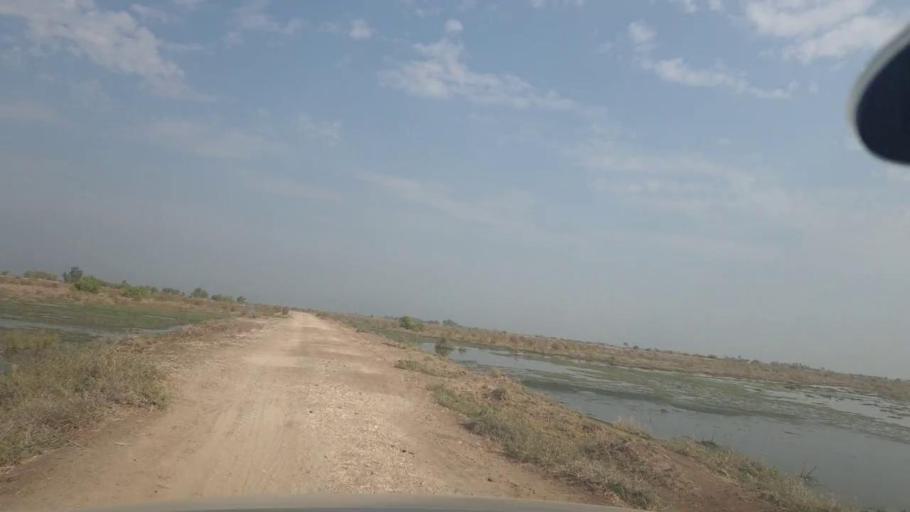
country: PK
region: Balochistan
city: Mehrabpur
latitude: 28.0300
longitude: 68.1313
